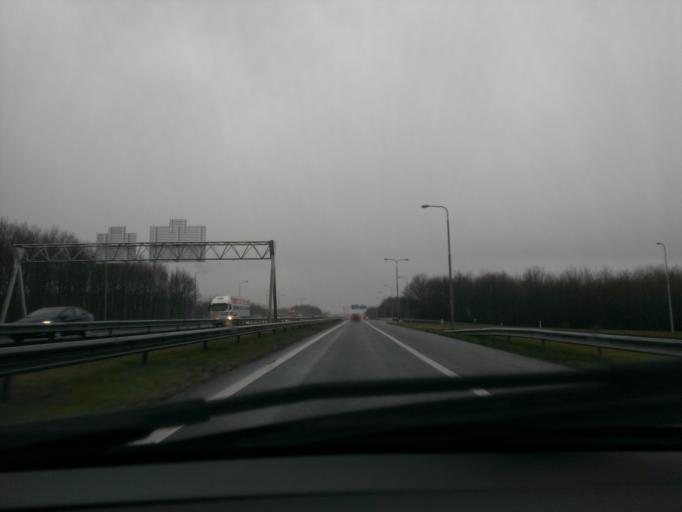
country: NL
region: Drenthe
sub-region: Gemeente Hoogeveen
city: Hoogeveen
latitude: 52.7094
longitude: 6.4594
